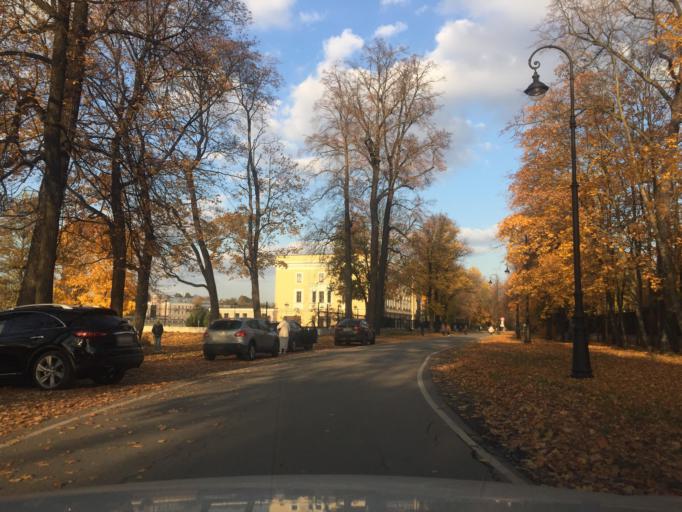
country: RU
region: St.-Petersburg
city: Novaya Derevnya
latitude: 59.9794
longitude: 30.2754
